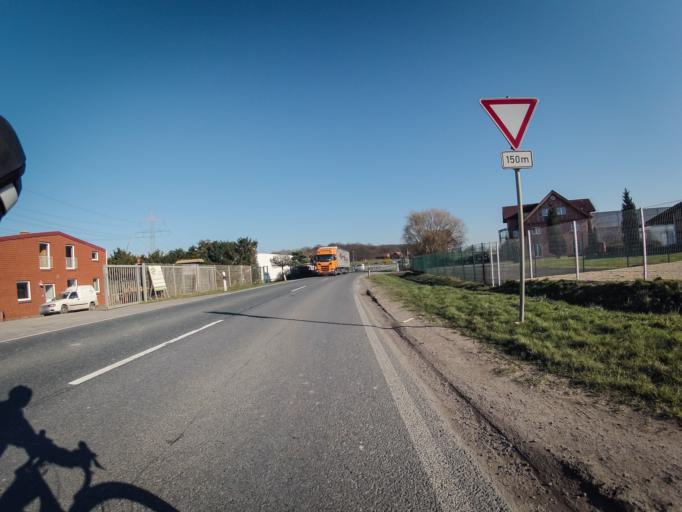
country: DE
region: North Rhine-Westphalia
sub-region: Regierungsbezirk Munster
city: Lotte
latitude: 52.2644
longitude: 7.8920
